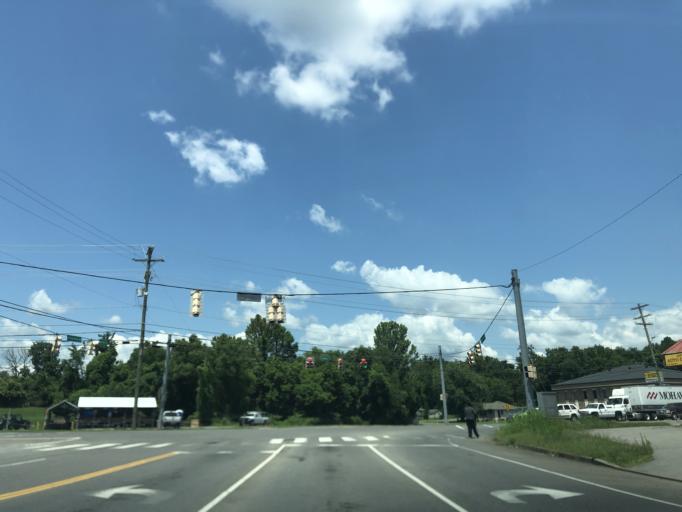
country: US
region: Tennessee
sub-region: Wilson County
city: Green Hill
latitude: 36.2149
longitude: -86.5886
